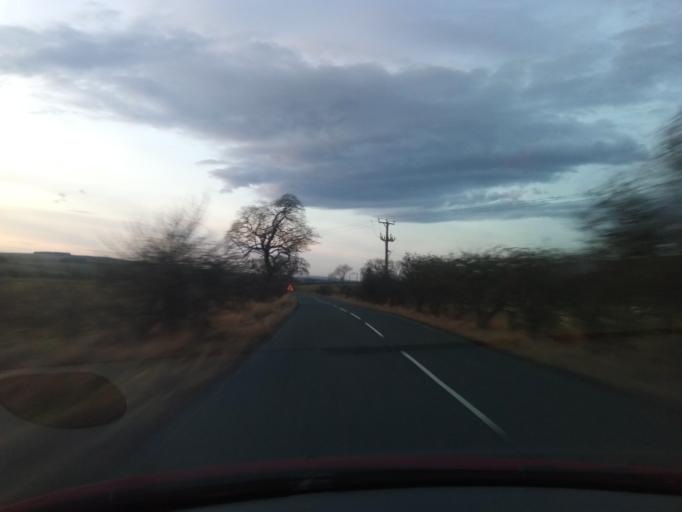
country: GB
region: England
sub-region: Northumberland
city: Otterburn
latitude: 55.2388
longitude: -2.2025
